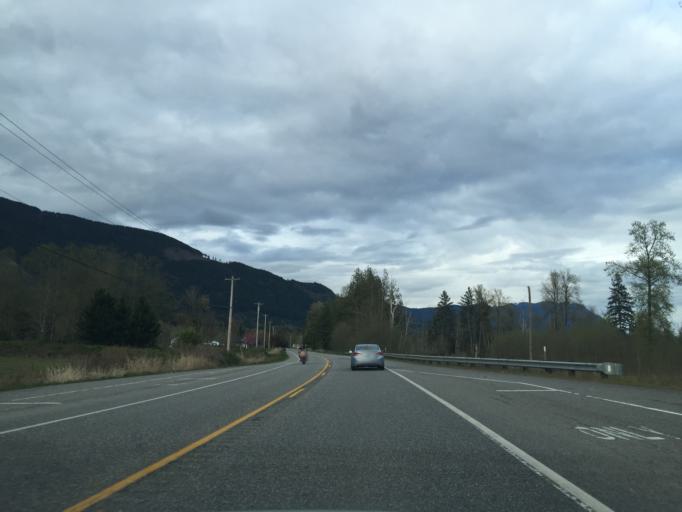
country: US
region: Washington
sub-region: Snohomish County
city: Arlington Heights
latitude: 48.2703
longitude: -122.0045
